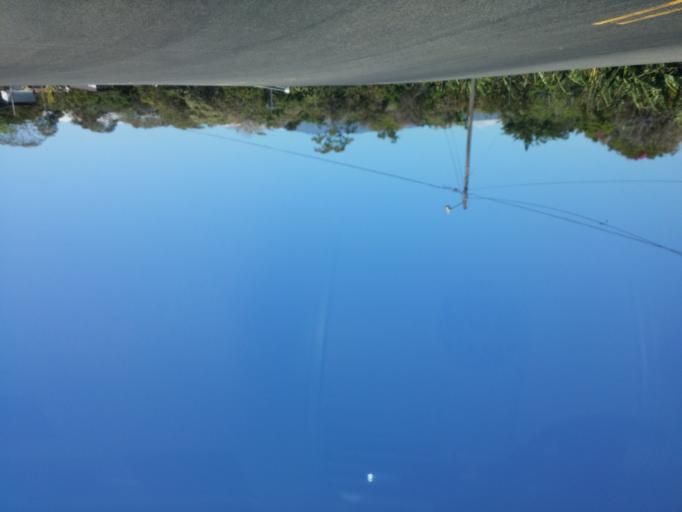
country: CR
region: Alajuela
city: Carrillos
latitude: 9.9972
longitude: -84.2693
